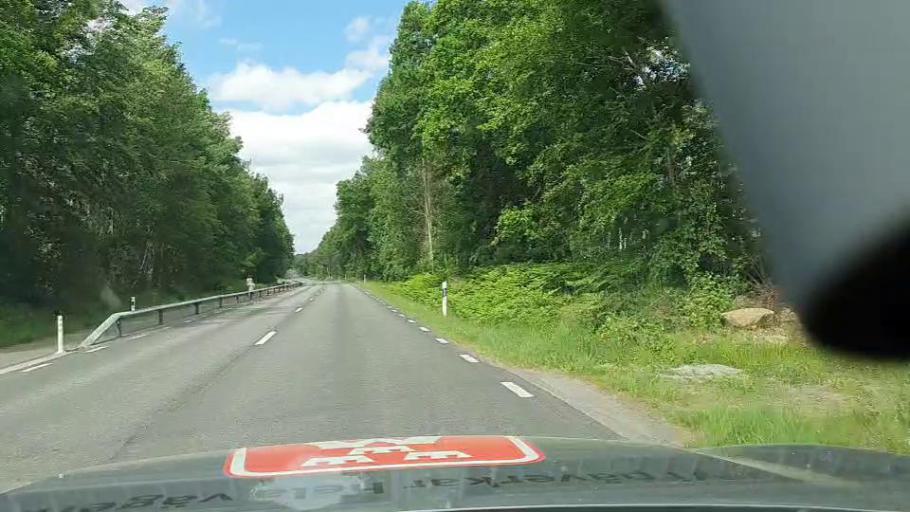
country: SE
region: Blekinge
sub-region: Karlshamns Kommun
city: Morrum
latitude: 56.1312
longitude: 14.6730
